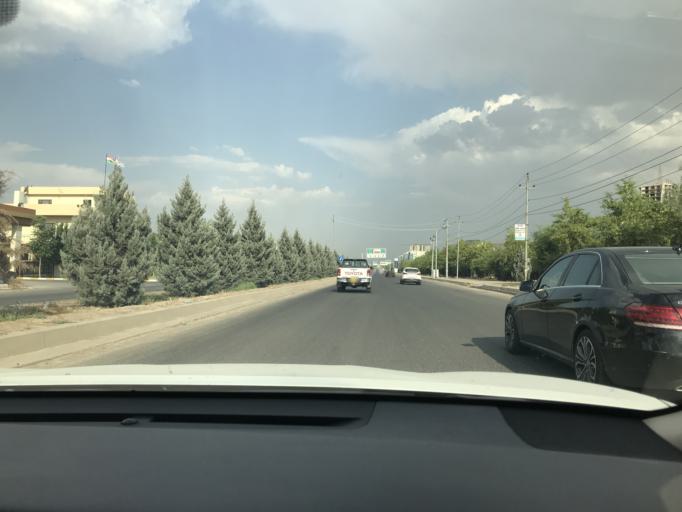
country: IQ
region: Arbil
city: Erbil
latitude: 36.2060
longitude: 43.9622
